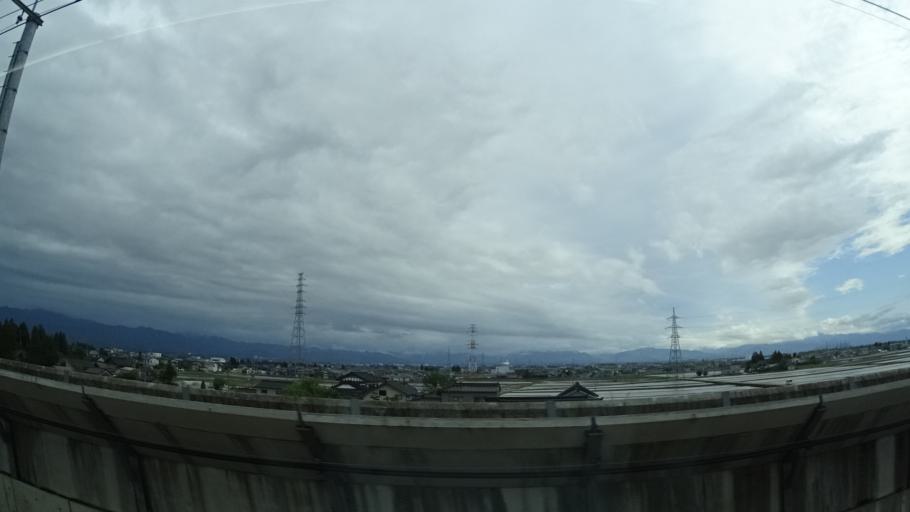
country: JP
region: Toyama
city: Namerikawa
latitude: 36.7119
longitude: 137.2952
